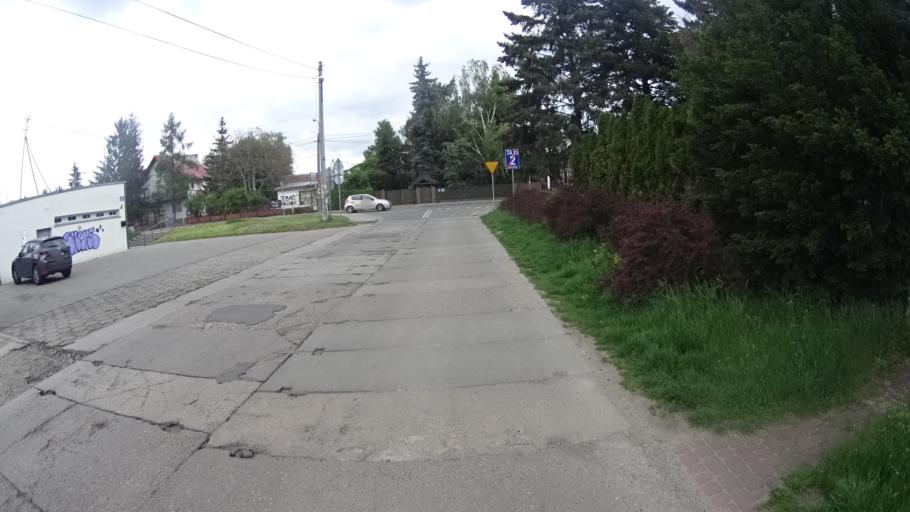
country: PL
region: Masovian Voivodeship
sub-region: Warszawa
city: Bemowo
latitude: 52.2855
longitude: 20.8874
